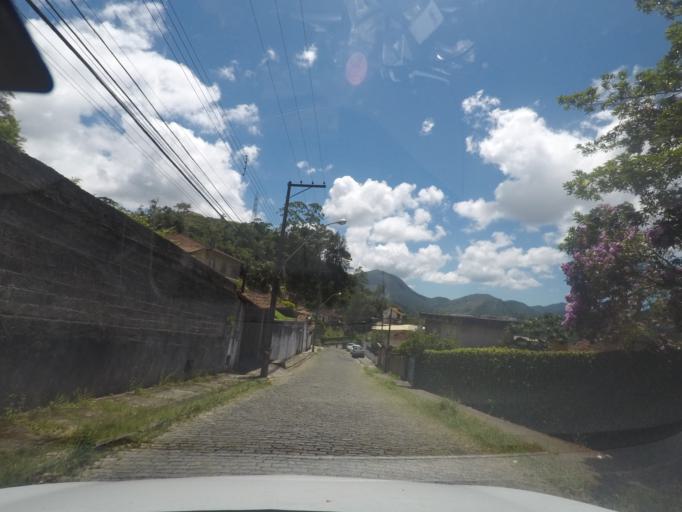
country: BR
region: Rio de Janeiro
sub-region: Teresopolis
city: Teresopolis
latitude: -22.4196
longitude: -42.9831
